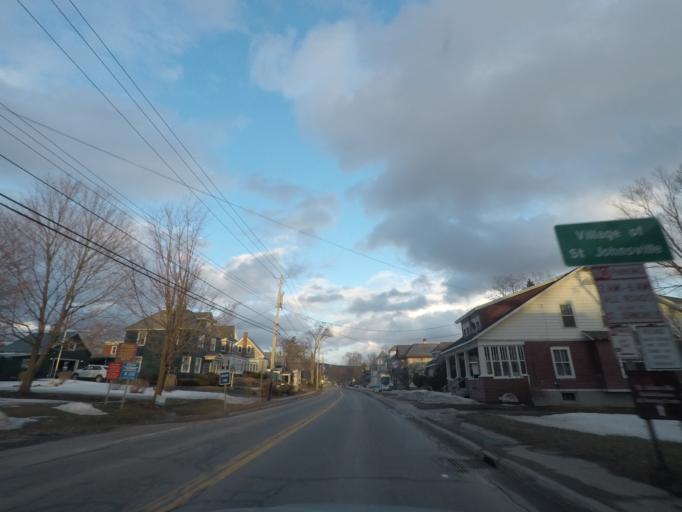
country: US
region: New York
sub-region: Montgomery County
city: Saint Johnsville
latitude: 42.9982
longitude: -74.6890
